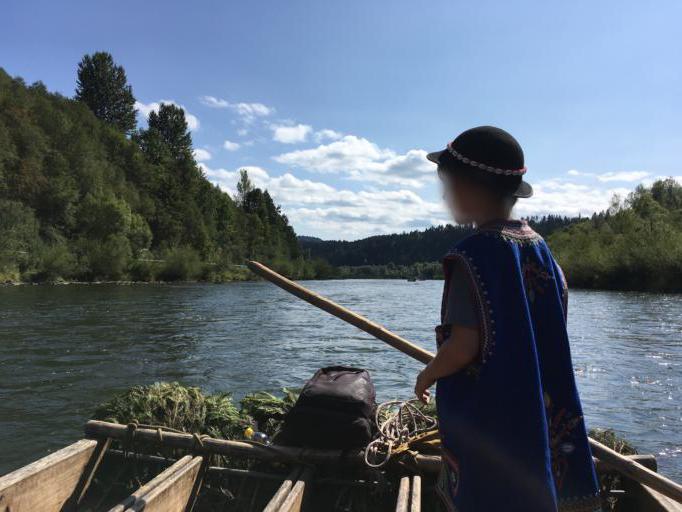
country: PL
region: Lesser Poland Voivodeship
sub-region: Powiat nowotarski
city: Kroscienko nad Dunajcem
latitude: 49.3994
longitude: 20.3816
